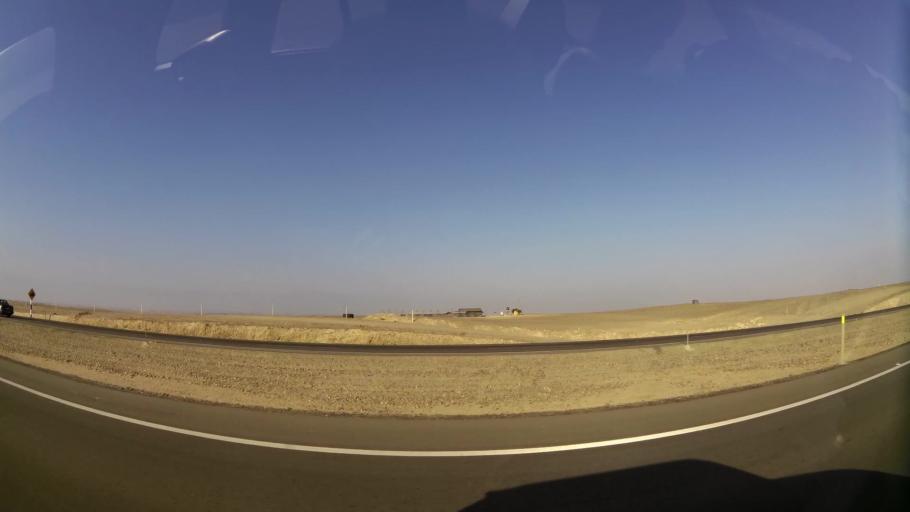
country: PE
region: Ica
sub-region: Provincia de Pisco
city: San Clemente
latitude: -13.6477
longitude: -76.1736
